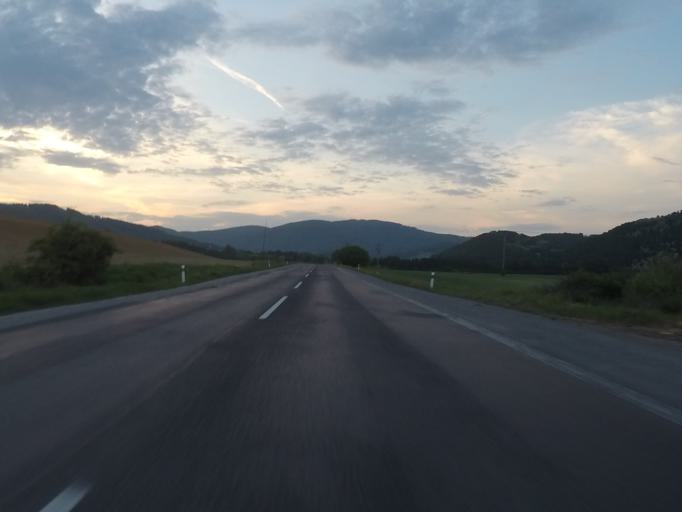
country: SK
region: Banskobystricky
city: Rimavska Sobota
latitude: 48.4852
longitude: 19.9446
